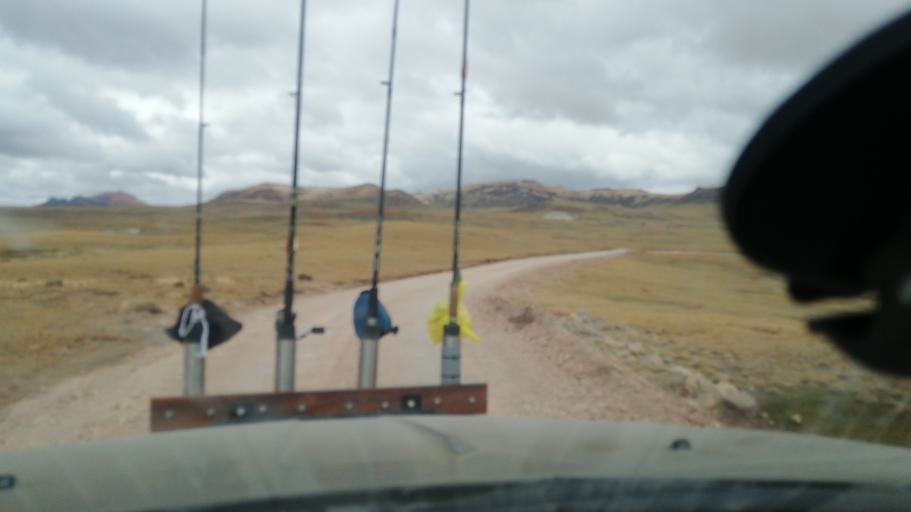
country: PE
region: Huancavelica
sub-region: Provincia de Huancavelica
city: Acobambilla
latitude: -12.5442
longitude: -75.5459
